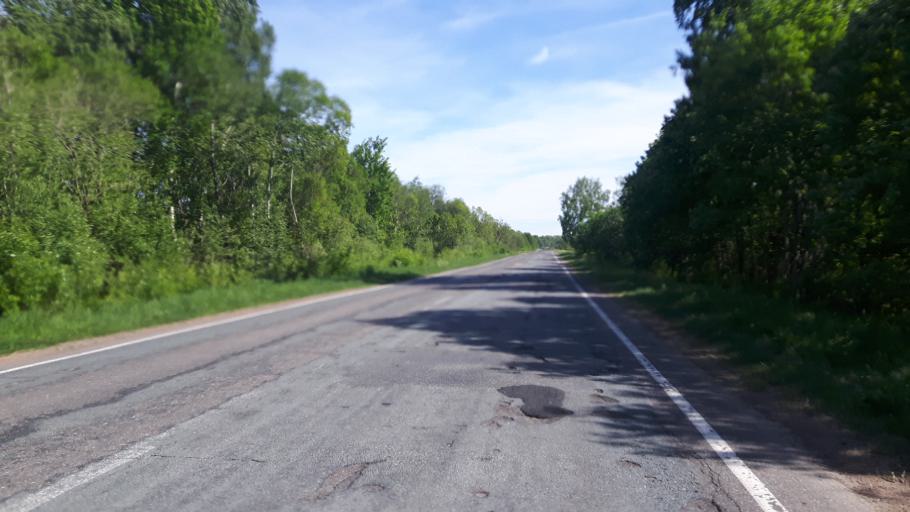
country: RU
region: Leningrad
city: Ivangorod
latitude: 59.4204
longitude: 28.3210
